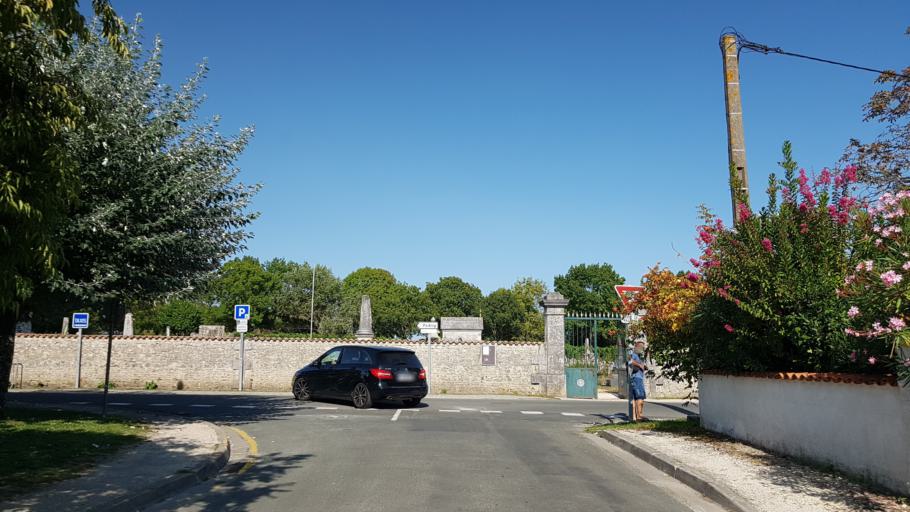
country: FR
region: Poitou-Charentes
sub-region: Departement de la Charente-Maritime
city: Breuillet
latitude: 45.7078
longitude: -1.0281
